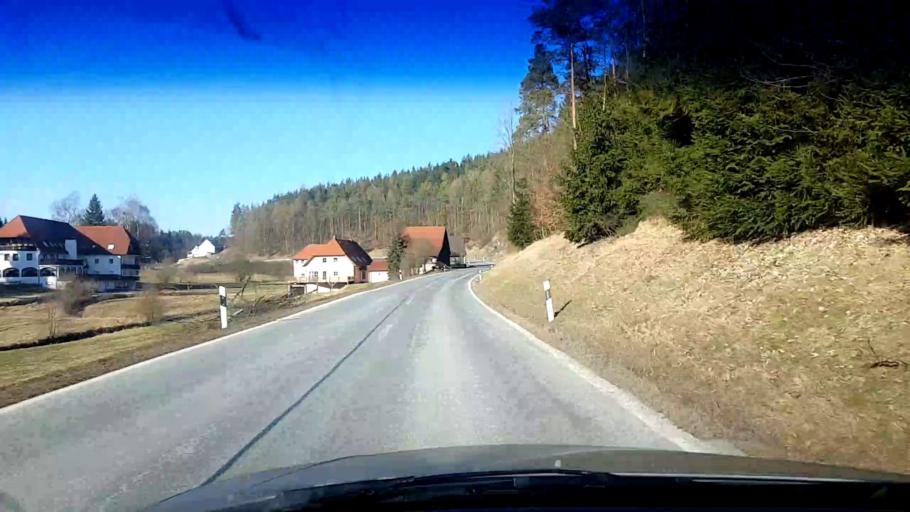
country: DE
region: Bavaria
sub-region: Upper Franconia
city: Aufsess
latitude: 49.9014
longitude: 11.2226
